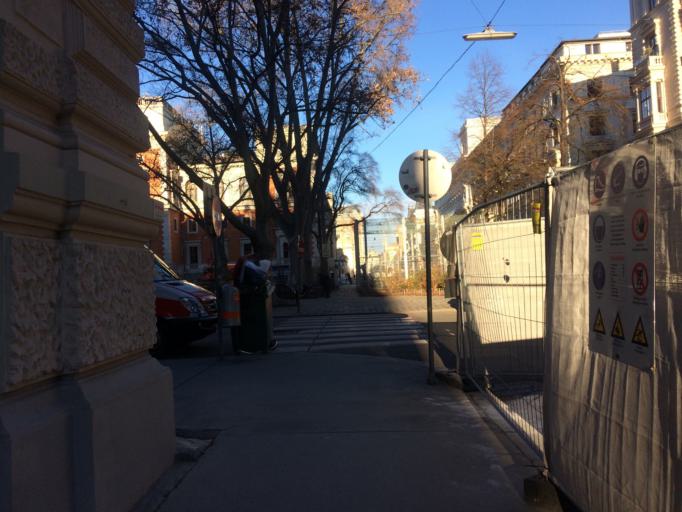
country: AT
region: Vienna
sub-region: Wien Stadt
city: Vienna
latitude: 48.2143
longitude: 16.3683
